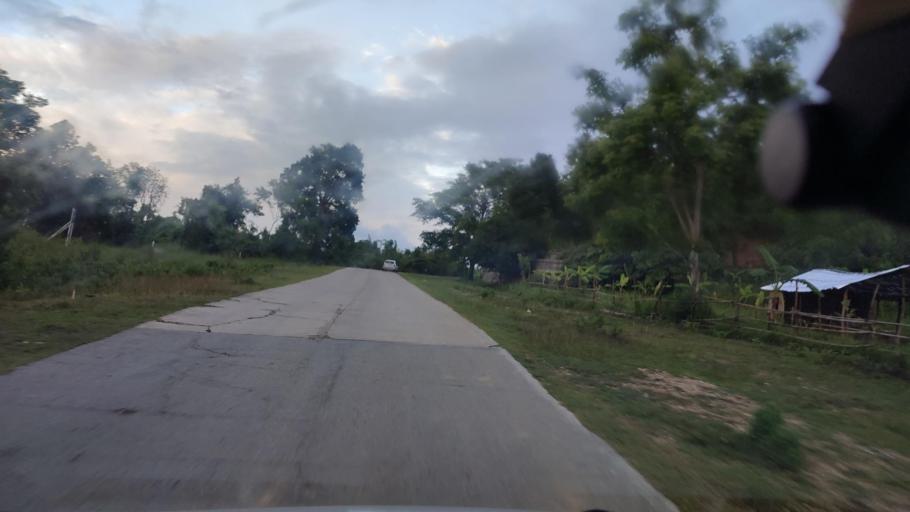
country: MM
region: Mandalay
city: Nay Pyi Taw
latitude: 19.9290
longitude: 95.9818
